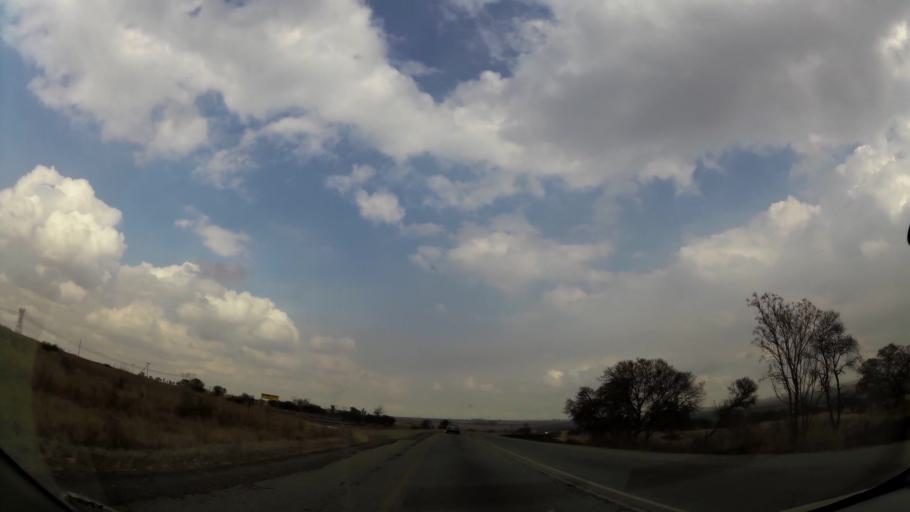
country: ZA
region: Orange Free State
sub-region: Fezile Dabi District Municipality
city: Sasolburg
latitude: -26.7934
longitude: 27.9167
